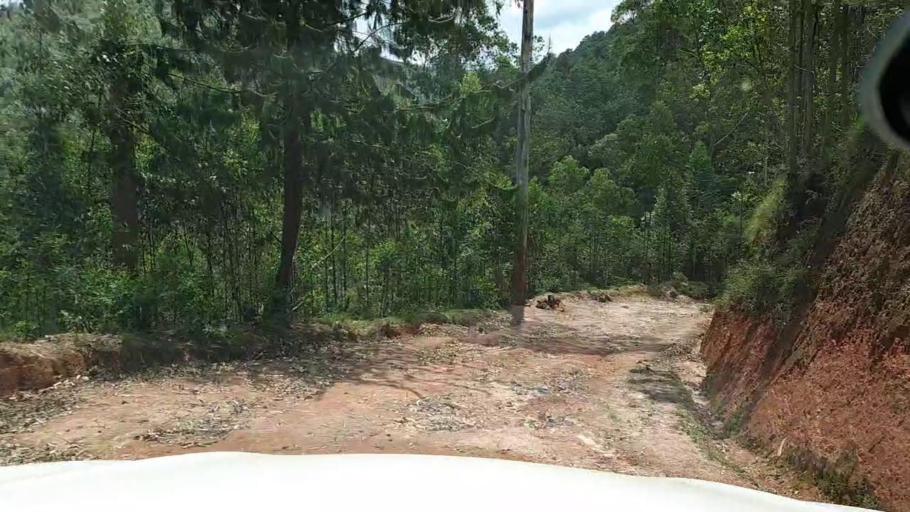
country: RW
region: Southern Province
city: Nzega
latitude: -2.6451
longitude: 29.4769
